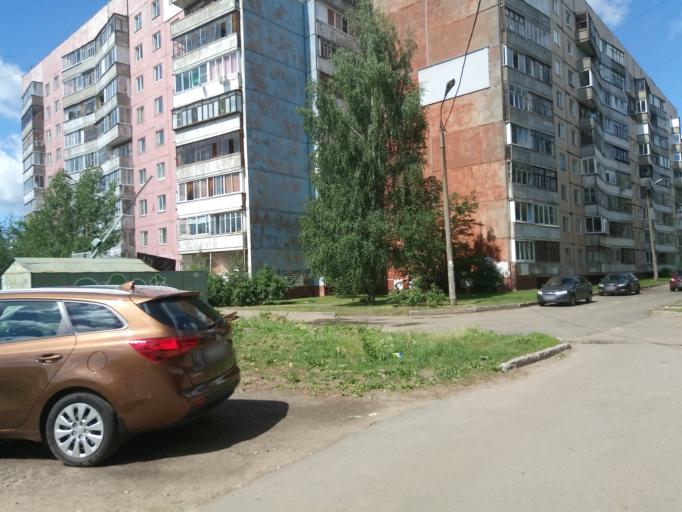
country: RU
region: Jaroslavl
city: Yaroslavl
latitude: 57.6503
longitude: 39.9646
